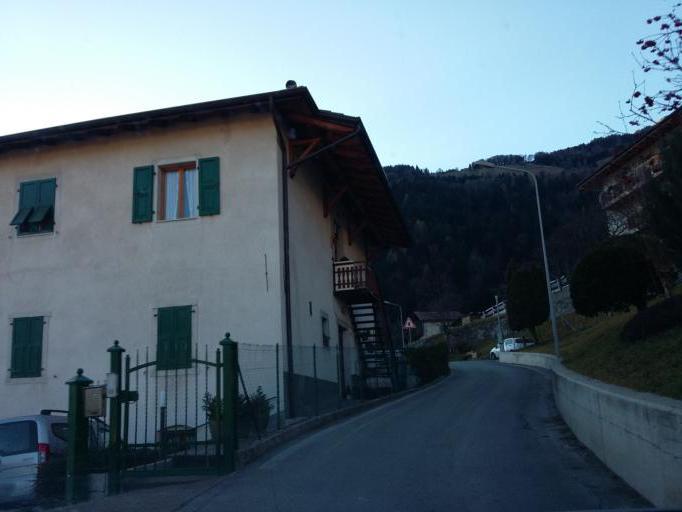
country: IT
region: Trentino-Alto Adige
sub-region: Provincia di Trento
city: Brione
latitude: 45.8946
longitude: 10.5889
